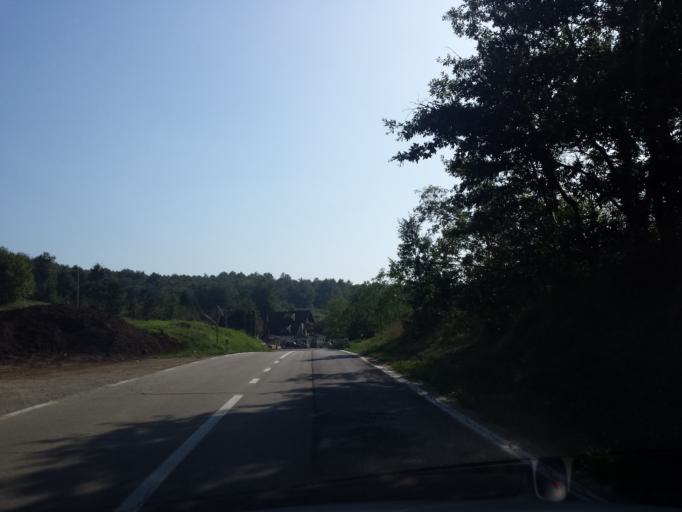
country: HR
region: Karlovacka
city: Ostarije
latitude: 45.2219
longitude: 15.3311
